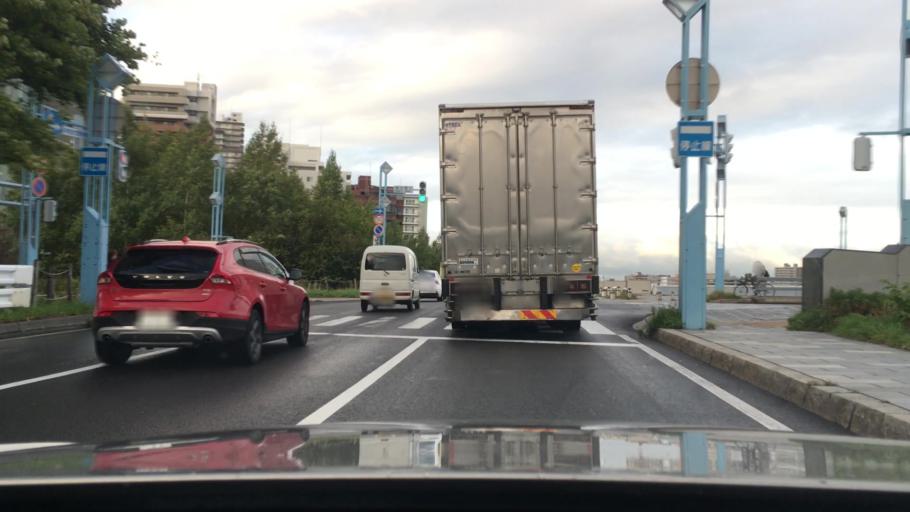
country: JP
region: Hokkaido
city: Sapporo
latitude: 43.0396
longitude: 141.3567
